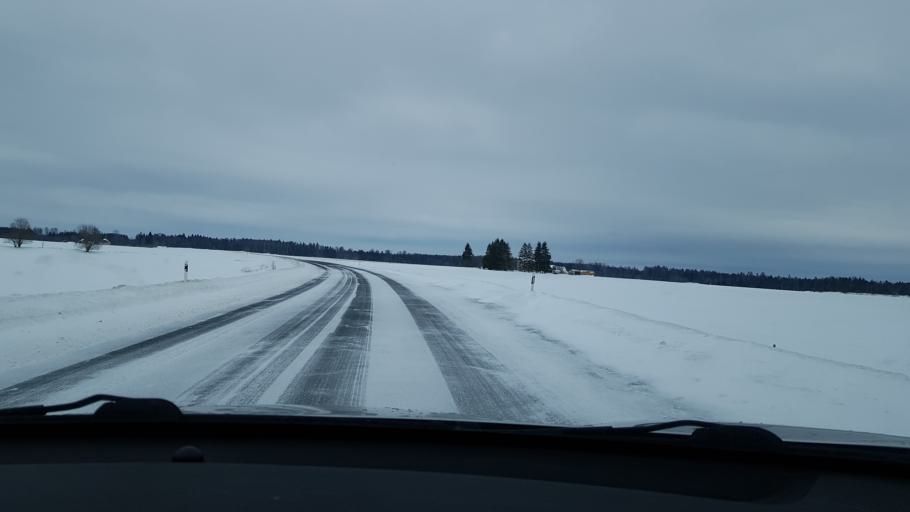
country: EE
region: Jaervamaa
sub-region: Jaerva-Jaani vald
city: Jarva-Jaani
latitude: 59.1126
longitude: 25.7957
